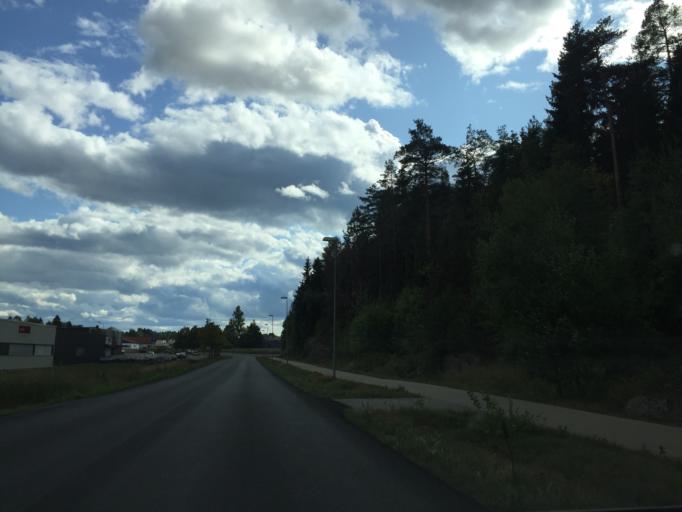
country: NO
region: Ostfold
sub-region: Askim
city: Askim
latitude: 59.5885
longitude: 11.1344
